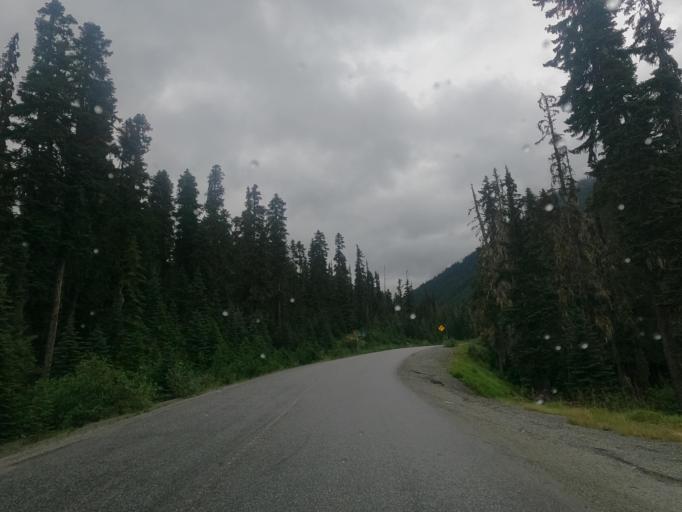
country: CA
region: British Columbia
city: Pemberton
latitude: 50.3851
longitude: -122.4672
